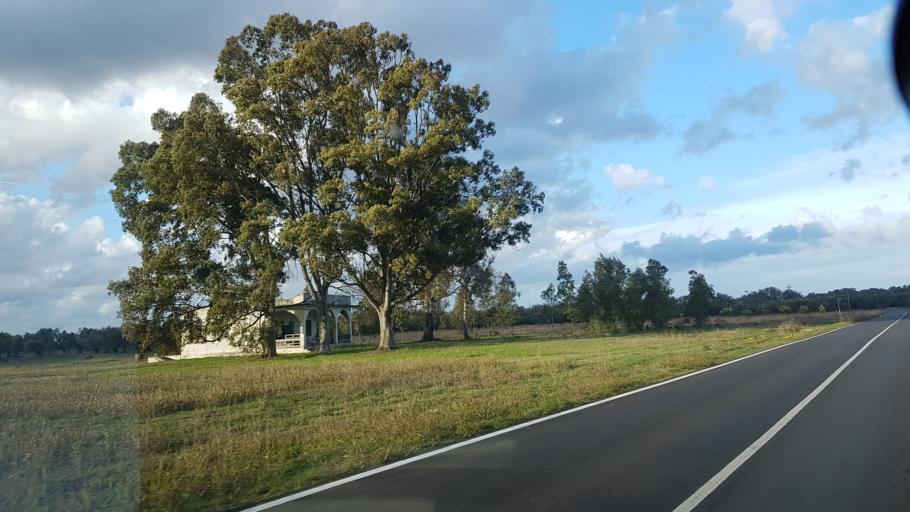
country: IT
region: Apulia
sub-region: Provincia di Brindisi
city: San Pietro Vernotico
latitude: 40.5033
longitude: 18.0065
